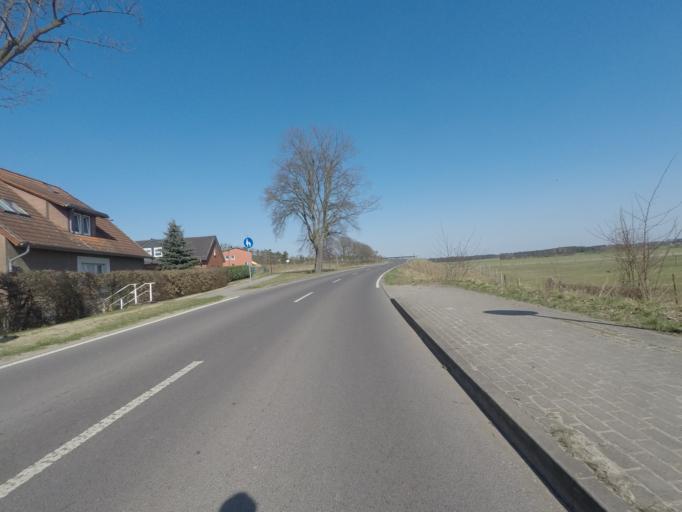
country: DE
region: Brandenburg
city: Marienwerder
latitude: 52.8578
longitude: 13.6821
